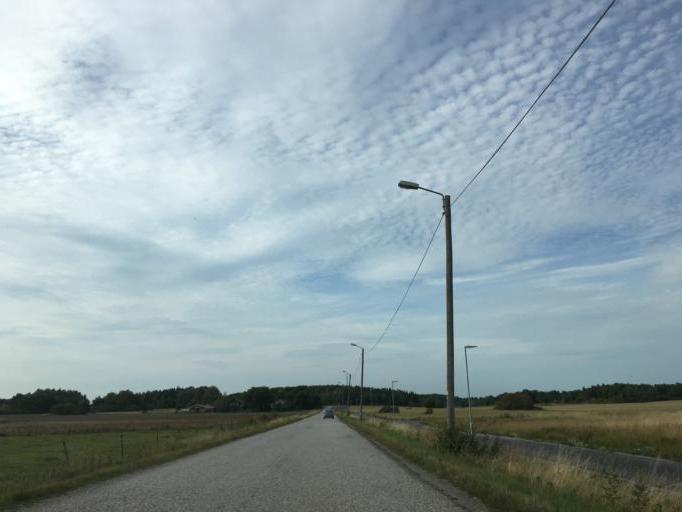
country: SE
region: Soedermanland
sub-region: Eskilstuna Kommun
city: Torshalla
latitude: 59.4399
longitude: 16.4740
